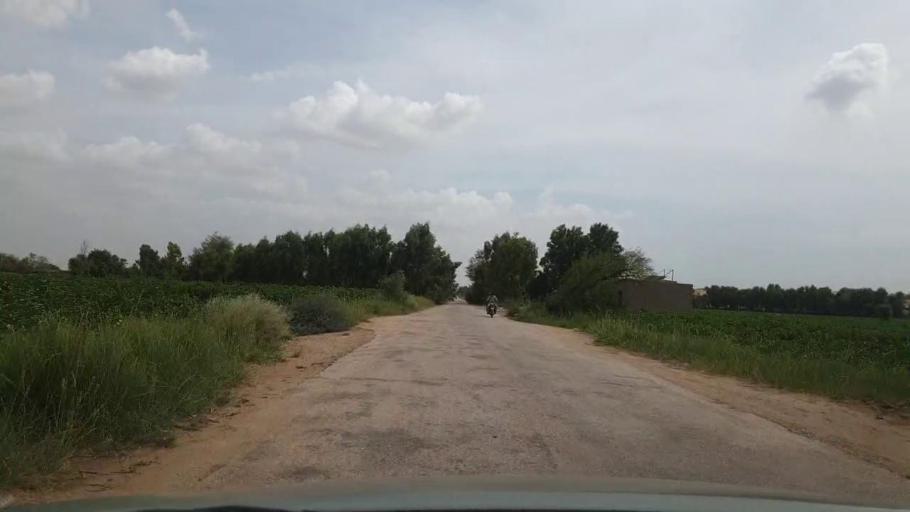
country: PK
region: Sindh
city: Kot Diji
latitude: 27.1621
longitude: 69.0350
